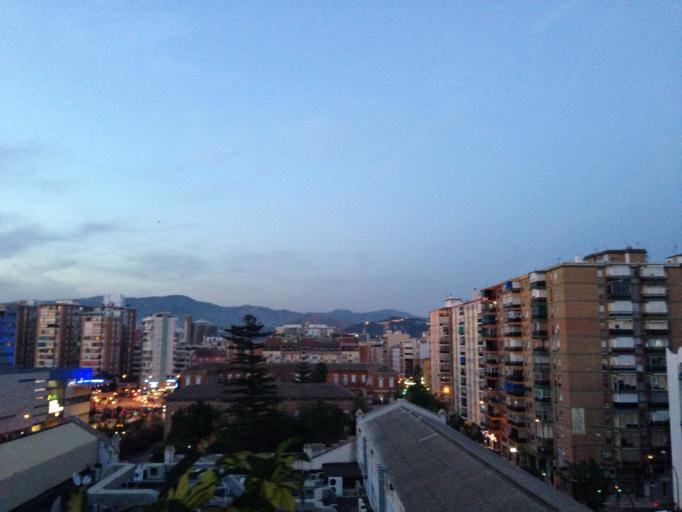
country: ES
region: Andalusia
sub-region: Provincia de Malaga
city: Malaga
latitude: 36.7098
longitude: -4.4321
